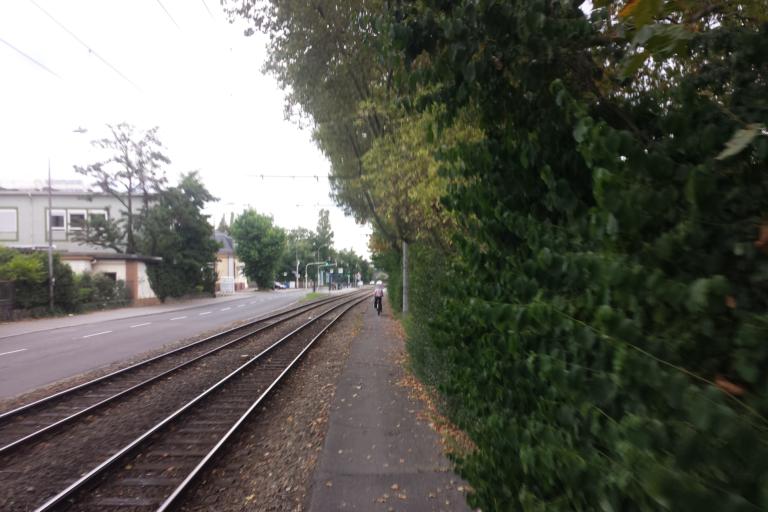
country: DE
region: Baden-Wuerttemberg
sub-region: Karlsruhe Region
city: Mannheim
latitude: 49.5266
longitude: 8.4705
